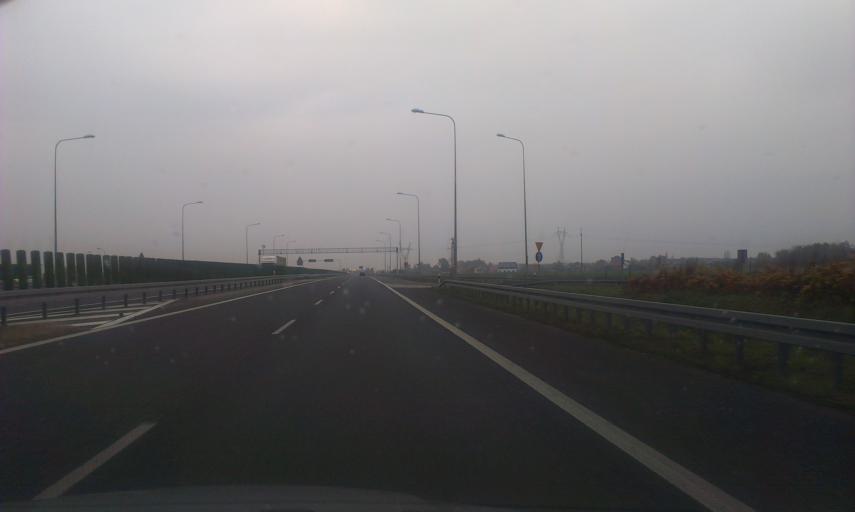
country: PL
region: Greater Poland Voivodeship
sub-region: Powiat poznanski
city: Rokietnica
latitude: 52.4964
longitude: 16.7549
